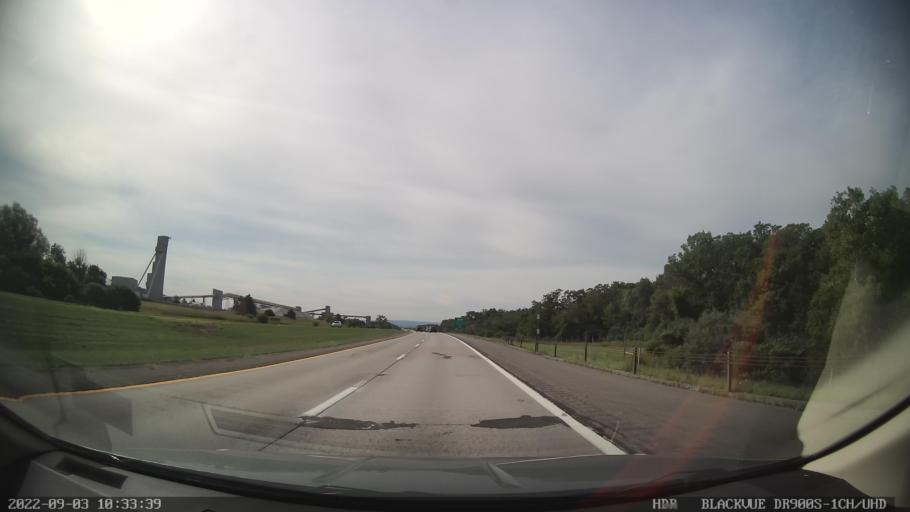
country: US
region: New York
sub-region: Livingston County
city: Mount Morris
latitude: 42.7527
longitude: -77.8400
